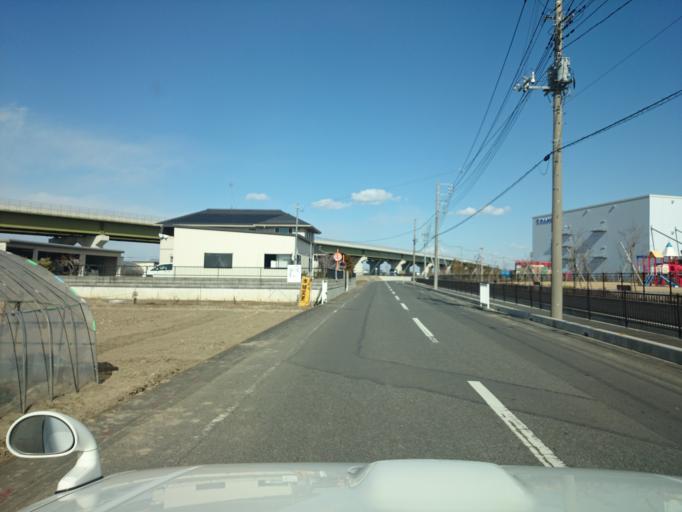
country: JP
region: Saitama
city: Satte
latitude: 36.0626
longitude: 139.7361
